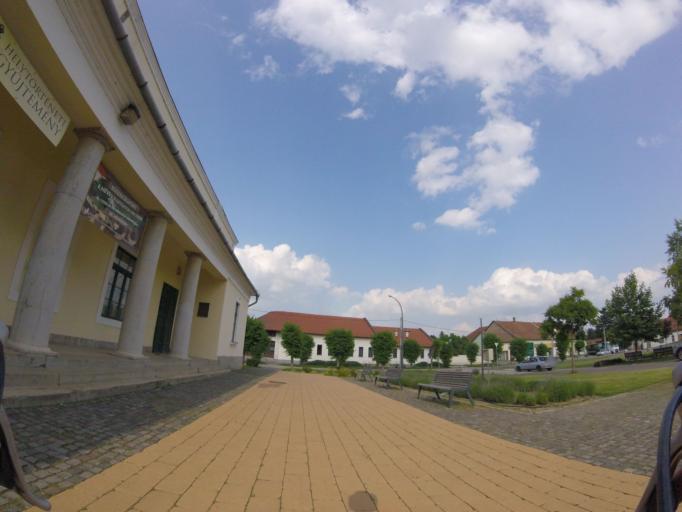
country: HU
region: Heves
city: Heves
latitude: 47.5952
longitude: 20.2881
